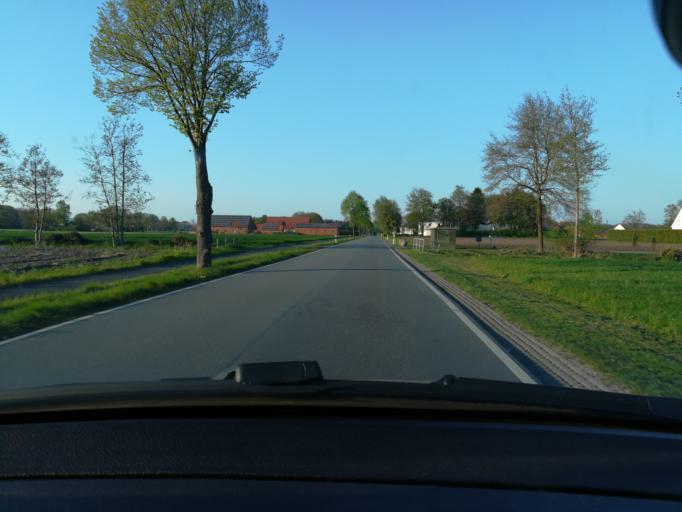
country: DE
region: North Rhine-Westphalia
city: Versmold
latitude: 52.0587
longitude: 8.1835
